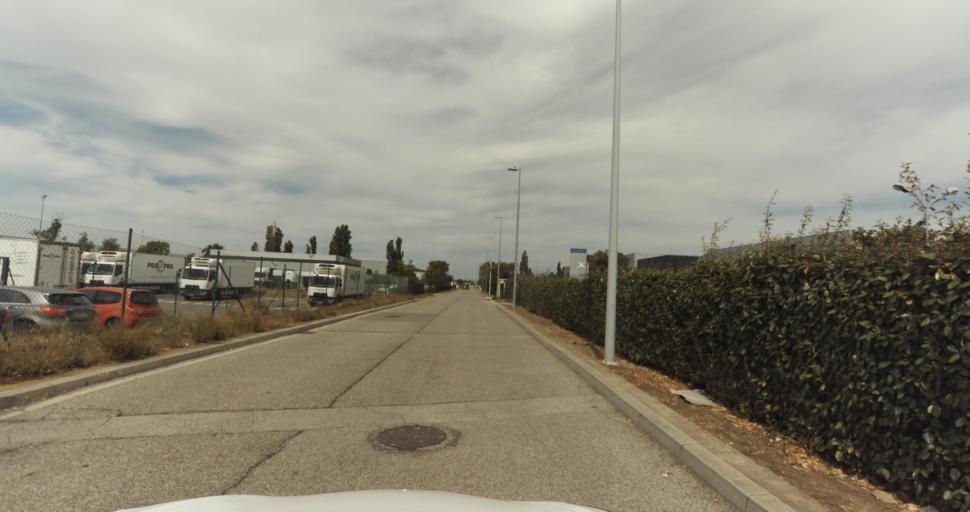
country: FR
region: Provence-Alpes-Cote d'Azur
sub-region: Departement des Bouches-du-Rhone
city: Miramas
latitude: 43.6052
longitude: 5.0024
